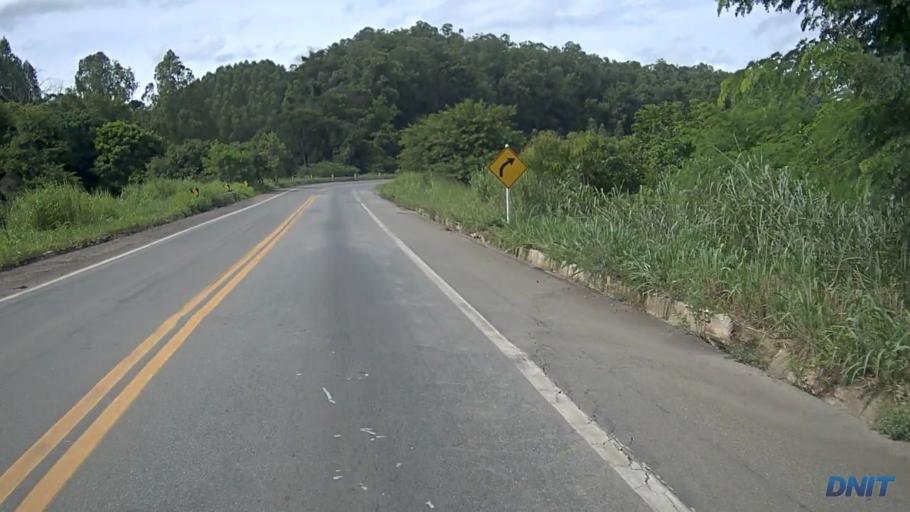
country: BR
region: Minas Gerais
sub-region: Ipaba
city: Ipaba
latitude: -19.3266
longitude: -42.4193
